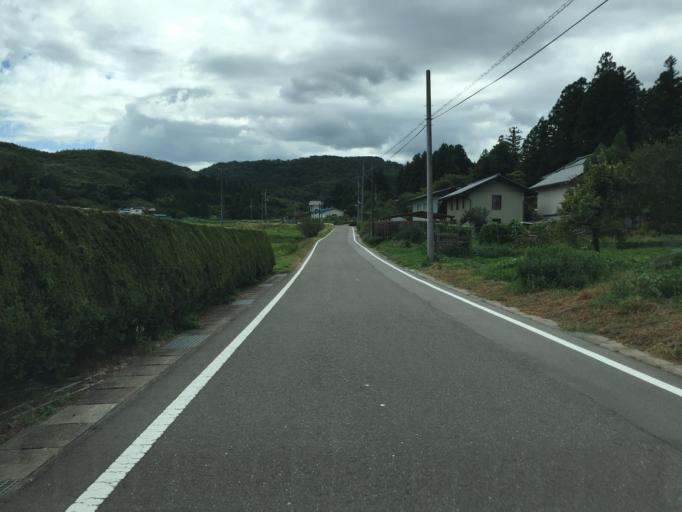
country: JP
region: Fukushima
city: Nihommatsu
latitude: 37.6557
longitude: 140.4233
